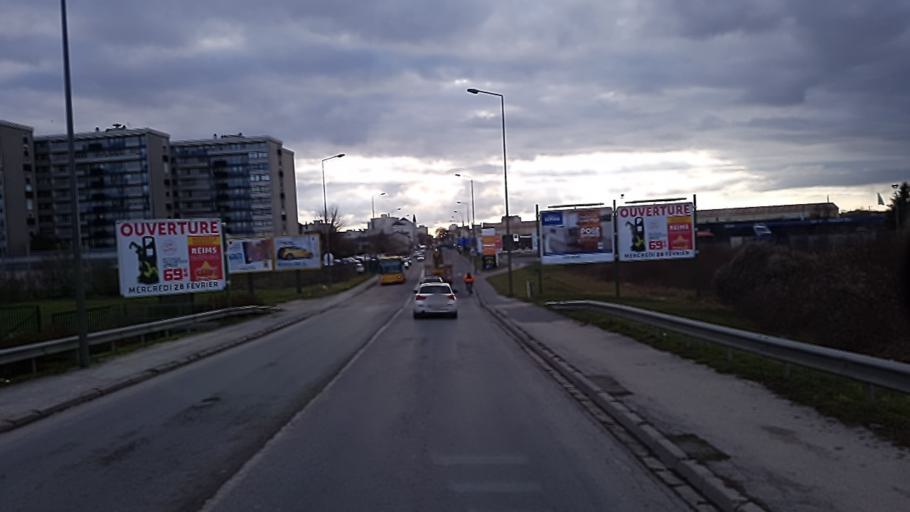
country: FR
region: Champagne-Ardenne
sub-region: Departement de la Marne
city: Betheny
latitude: 49.2666
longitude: 4.0640
